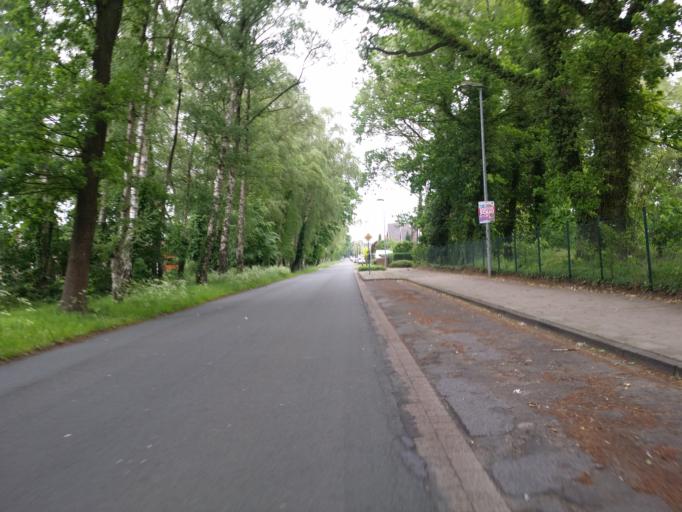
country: DE
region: Lower Saxony
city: Ganderkesee
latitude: 53.0384
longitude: 8.5314
